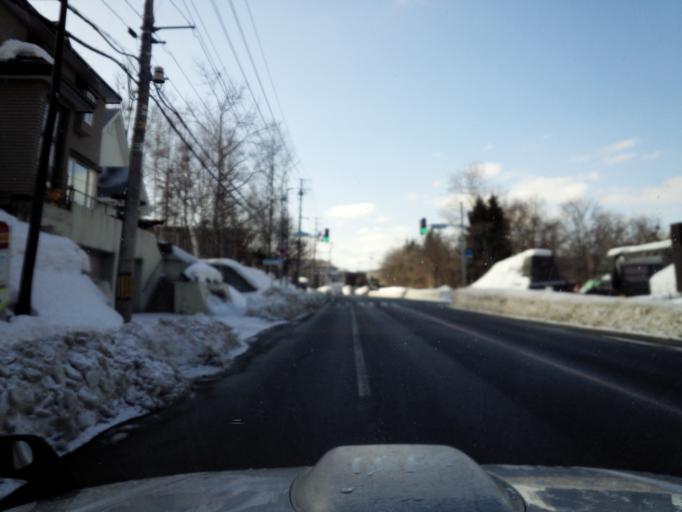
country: JP
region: Hokkaido
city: Sapporo
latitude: 42.9409
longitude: 141.3447
